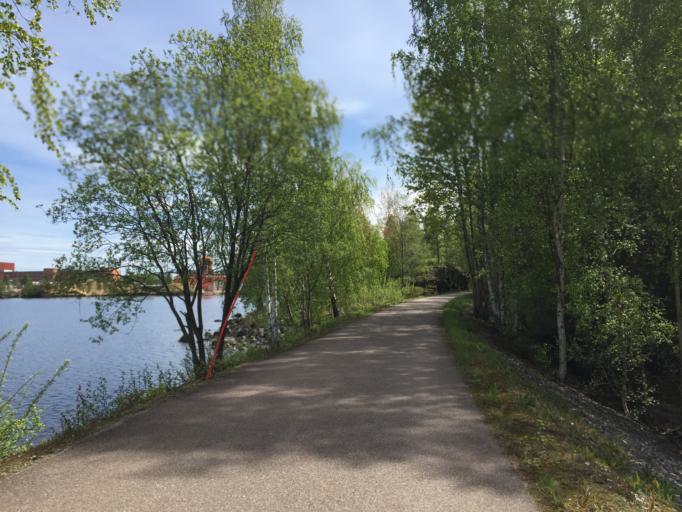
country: SE
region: Dalarna
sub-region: Ludvika Kommun
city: Ludvika
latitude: 60.1447
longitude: 15.1574
